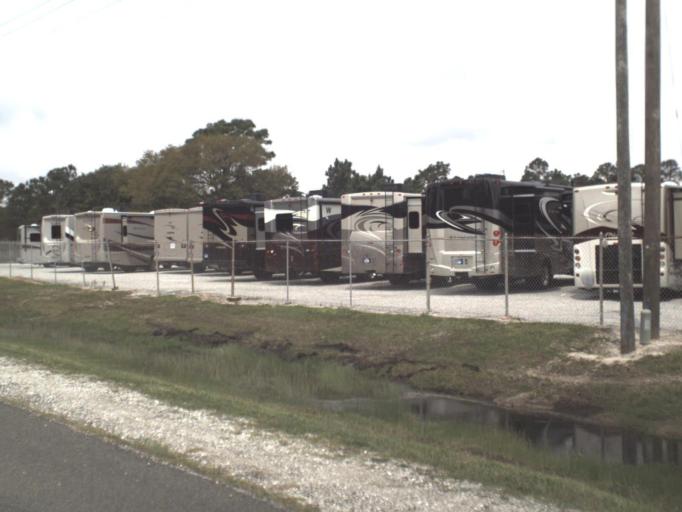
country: US
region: Florida
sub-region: Santa Rosa County
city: Woodlawn Beach
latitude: 30.4039
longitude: -86.9632
